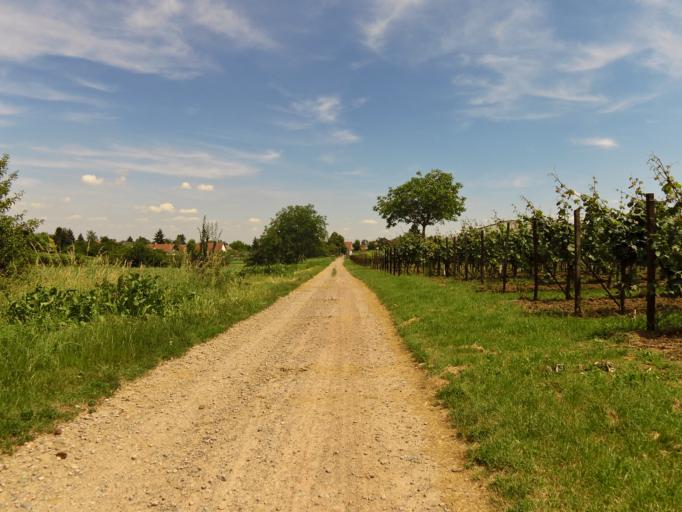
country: DE
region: Rheinland-Pfalz
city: Walsheim
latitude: 49.2349
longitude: 8.1175
